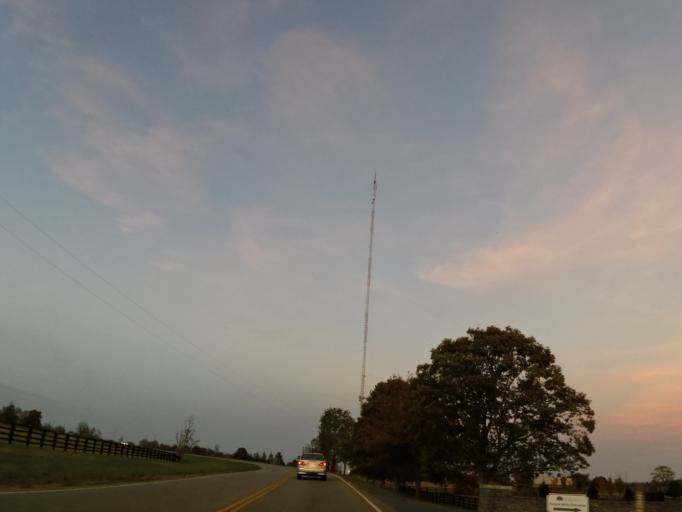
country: US
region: Kentucky
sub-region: Fayette County
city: Lexington-Fayette
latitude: 38.0317
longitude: -84.3972
